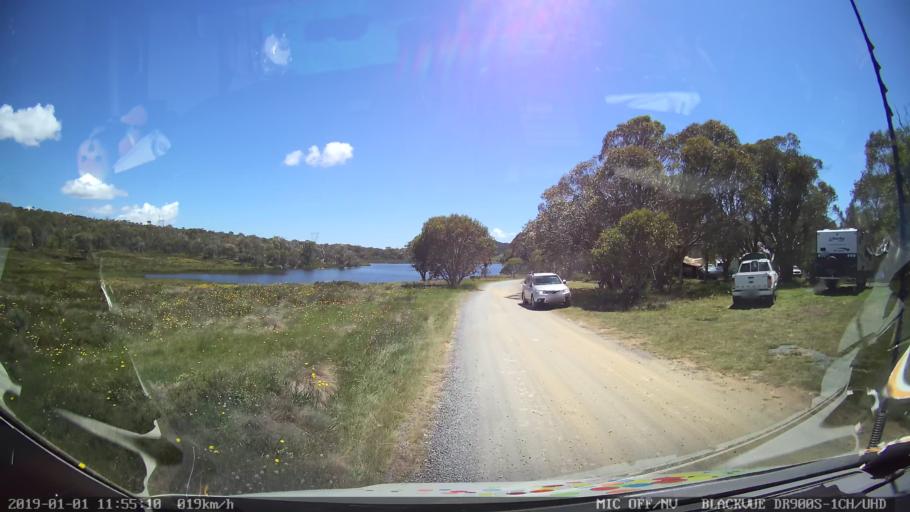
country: AU
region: New South Wales
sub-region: Snowy River
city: Jindabyne
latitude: -35.8891
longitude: 148.4484
